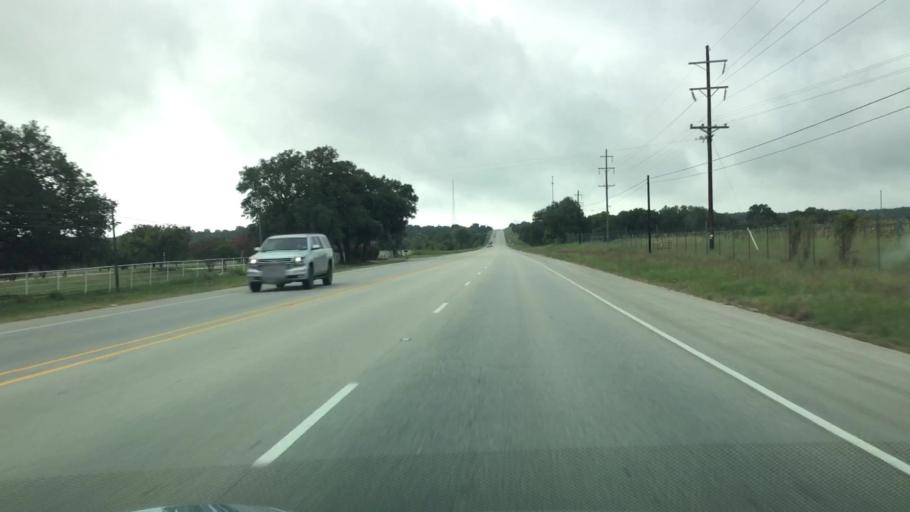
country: US
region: Texas
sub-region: Blanco County
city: Blanco
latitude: 30.0618
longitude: -98.4112
